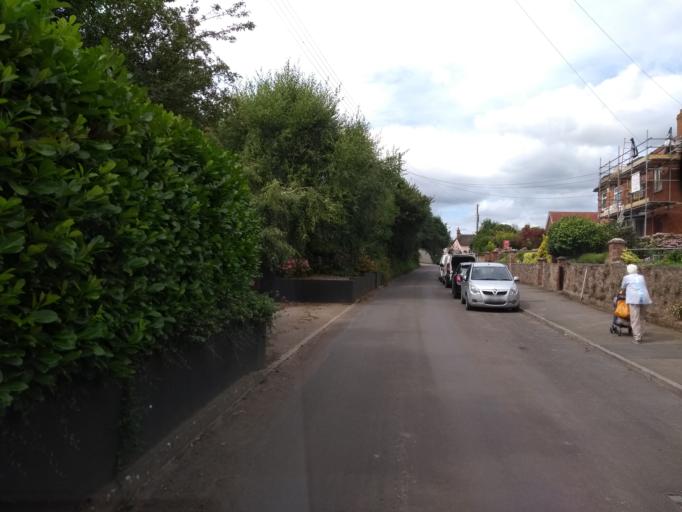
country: GB
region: England
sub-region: Somerset
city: North Petherton
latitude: 51.0906
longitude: -3.0204
